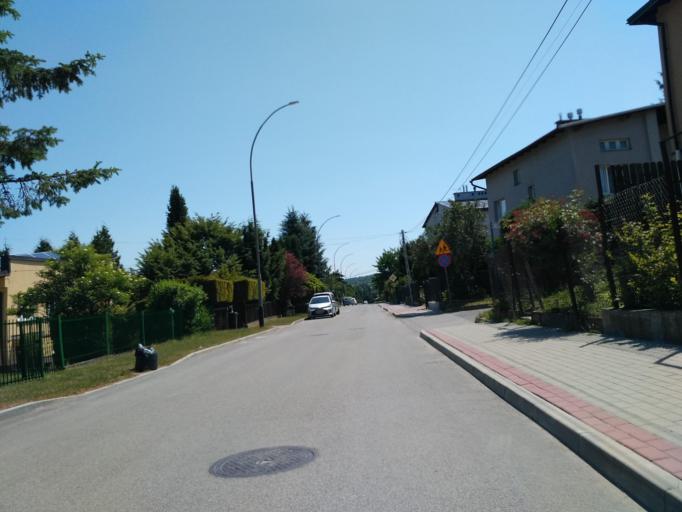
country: PL
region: Subcarpathian Voivodeship
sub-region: Krosno
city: Krosno
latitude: 49.6985
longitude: 21.7772
